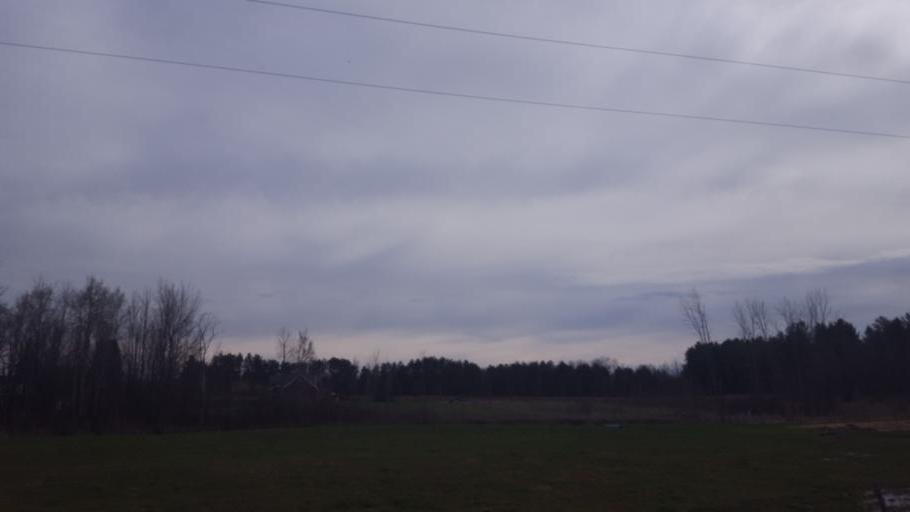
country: US
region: Michigan
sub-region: Clare County
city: Clare
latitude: 43.8729
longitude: -84.7283
